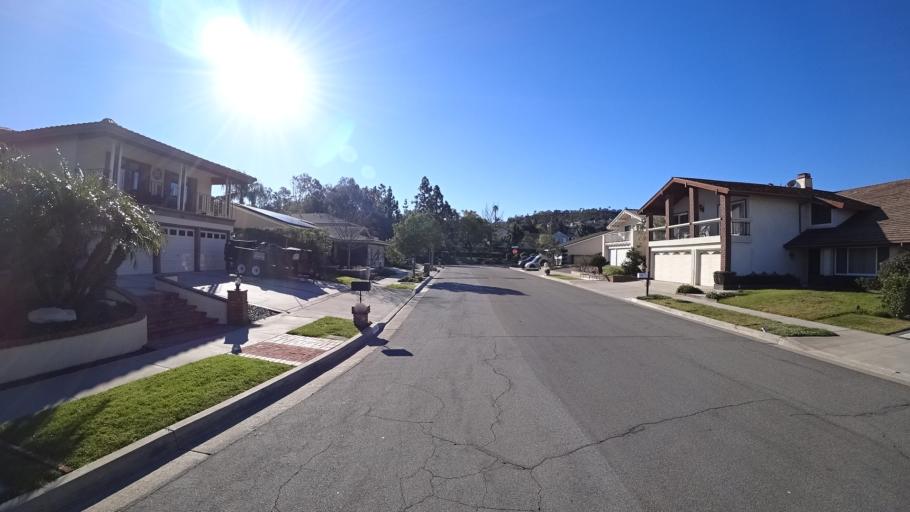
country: US
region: California
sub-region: Orange County
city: Villa Park
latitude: 33.8448
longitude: -117.8027
